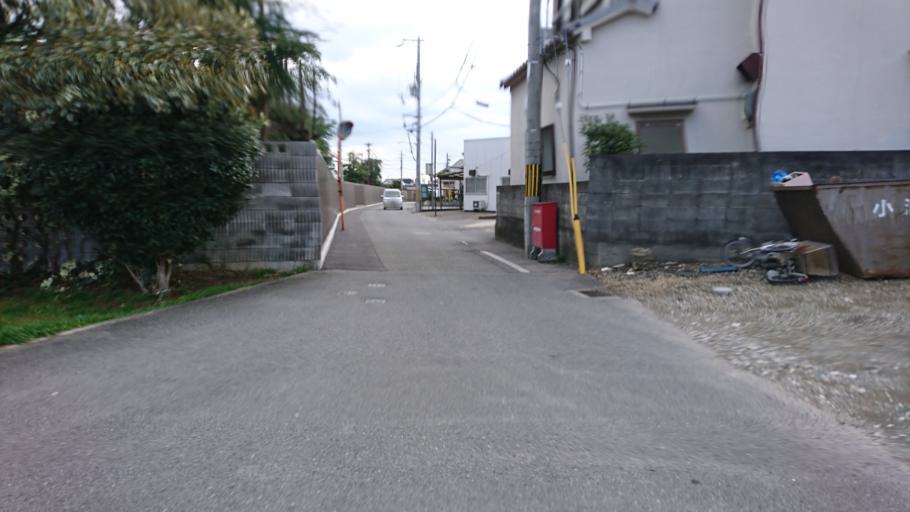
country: JP
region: Hyogo
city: Kakogawacho-honmachi
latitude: 34.7799
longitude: 134.8245
